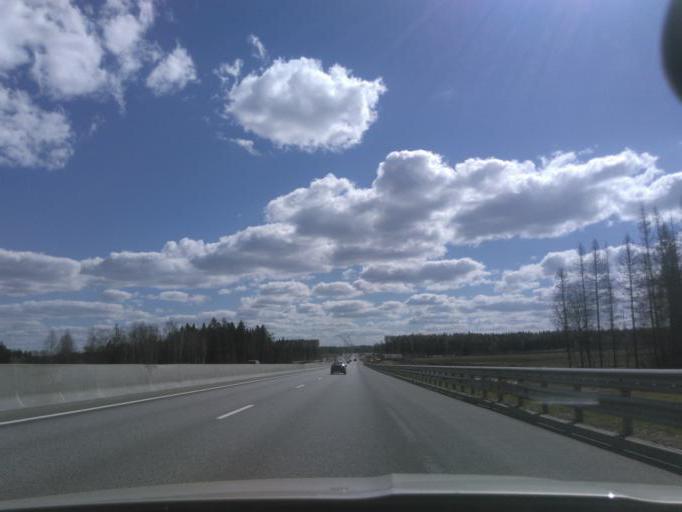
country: RU
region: Moskovskaya
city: Radumlya
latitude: 56.1018
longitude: 37.1524
